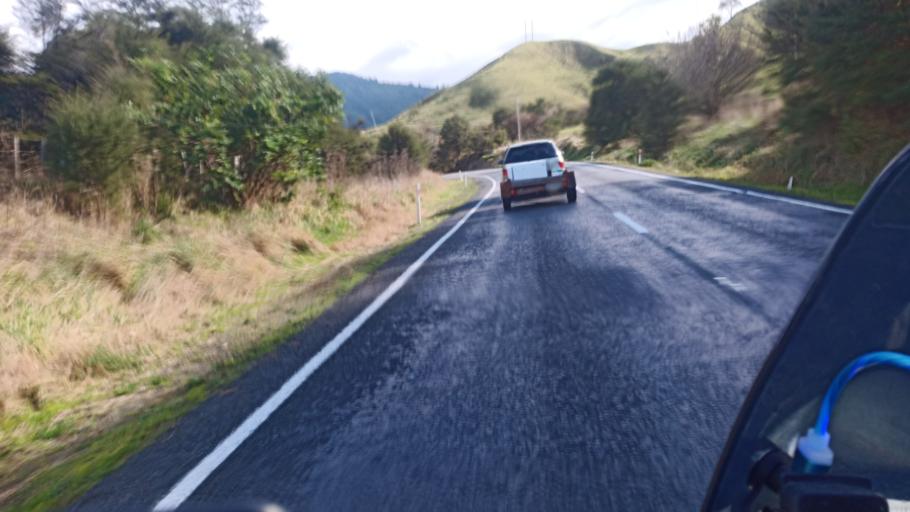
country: NZ
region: Gisborne
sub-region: Gisborne District
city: Gisborne
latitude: -38.1206
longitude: 178.3096
